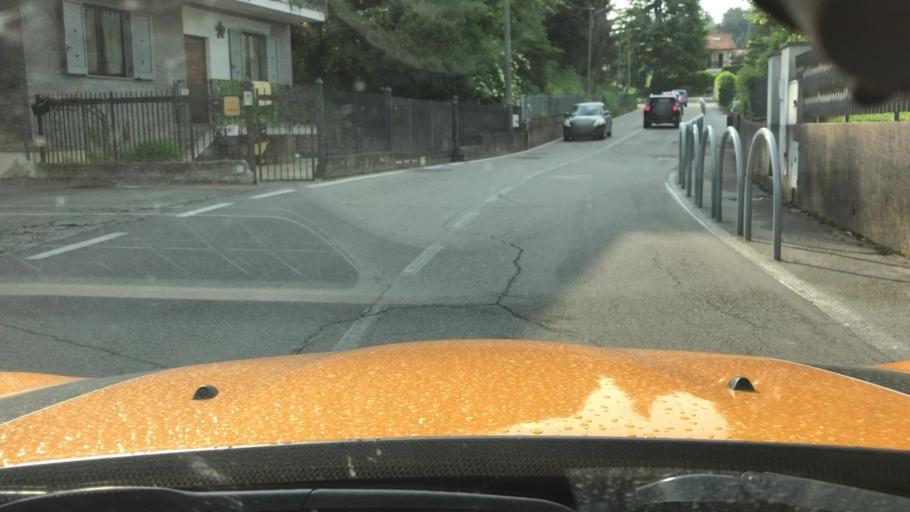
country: IT
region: Lombardy
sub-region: Provincia di Como
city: Senna Comasco
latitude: 45.7632
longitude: 9.1106
